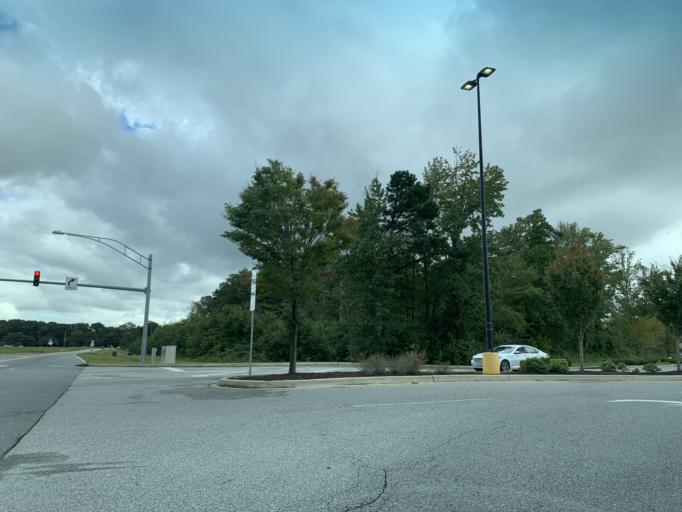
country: US
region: Maryland
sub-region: Caroline County
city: Denton
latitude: 38.8755
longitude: -75.8201
